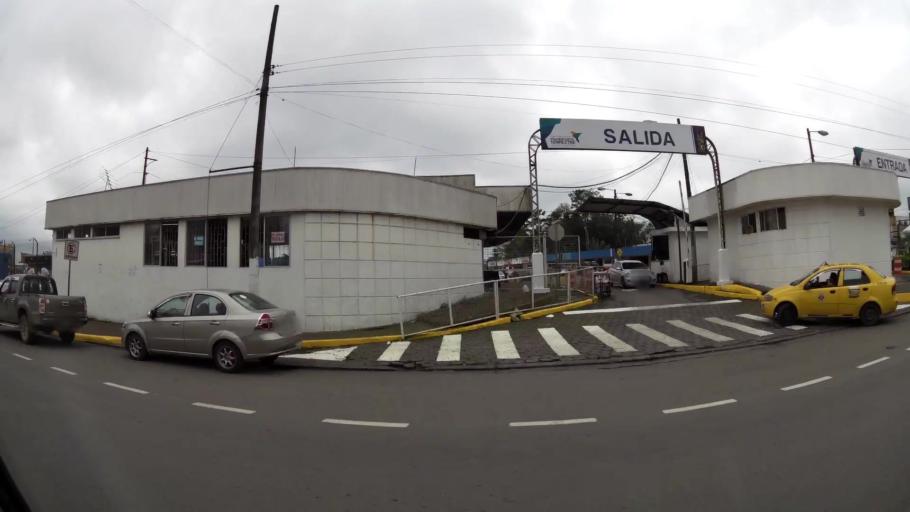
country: EC
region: Santo Domingo de los Tsachilas
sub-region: Canton Santo Domingo de los Colorados
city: Santo Domingo de los Colorados
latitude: -0.2394
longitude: -79.1709
